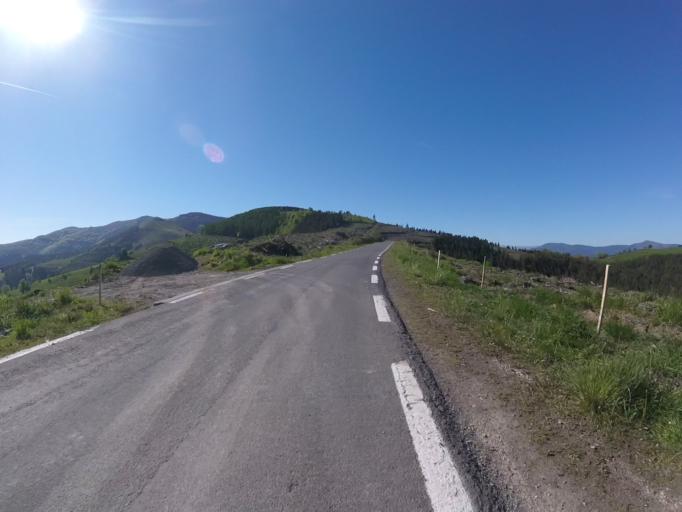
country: ES
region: Basque Country
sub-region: Provincia de Guipuzcoa
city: Errezil
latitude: 43.2053
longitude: -2.1982
